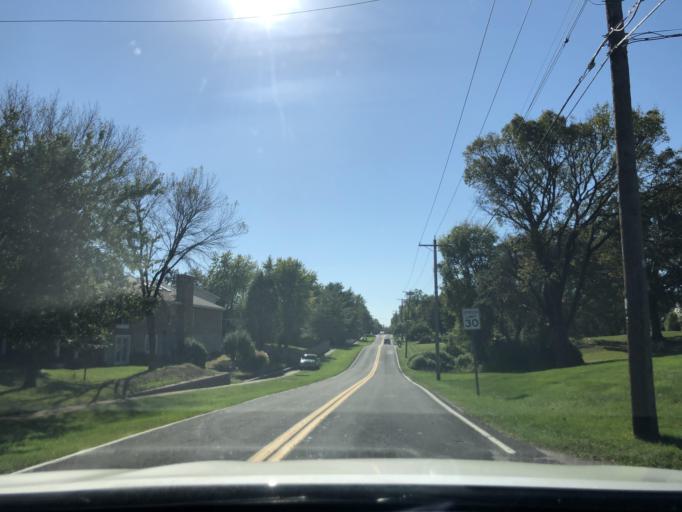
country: US
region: Missouri
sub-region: Saint Louis County
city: Concord
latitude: 38.4890
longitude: -90.3619
